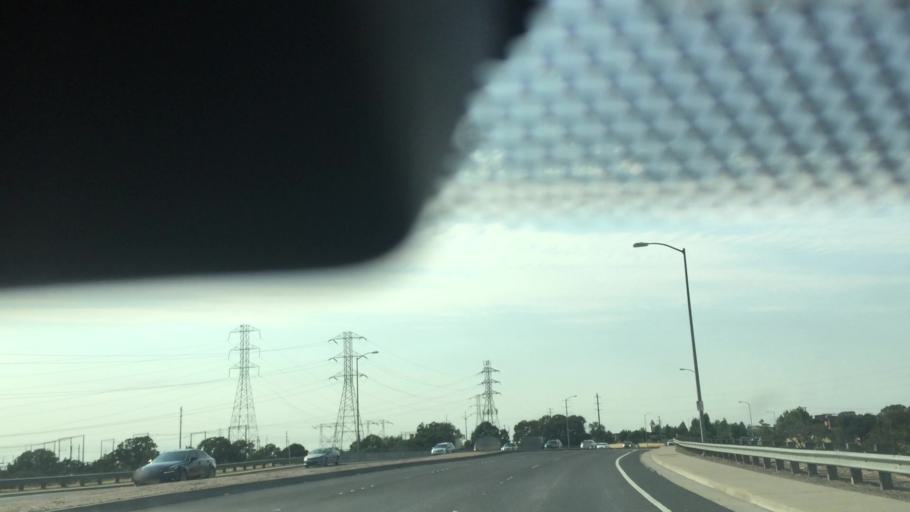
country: US
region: California
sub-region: Placer County
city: Roseville
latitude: 38.7635
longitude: -121.2595
